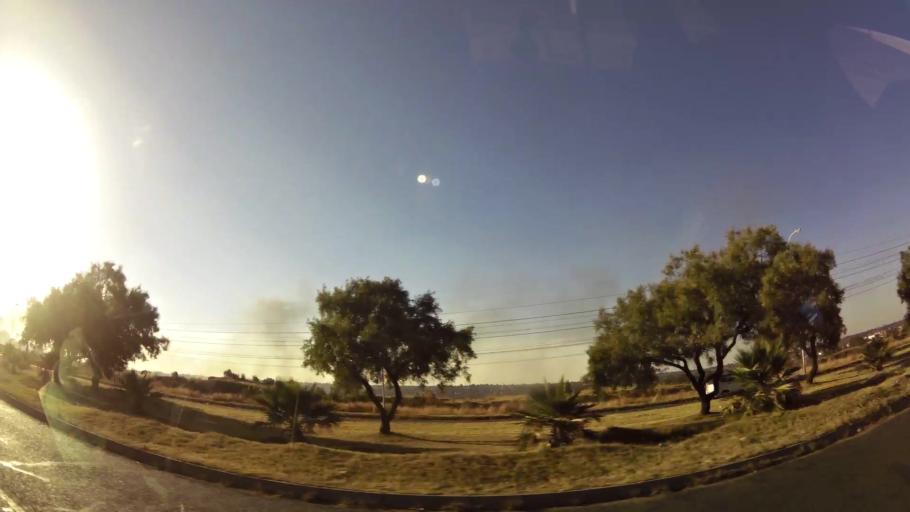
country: ZA
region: Gauteng
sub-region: City of Johannesburg Metropolitan Municipality
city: Roodepoort
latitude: -26.1805
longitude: 27.8863
